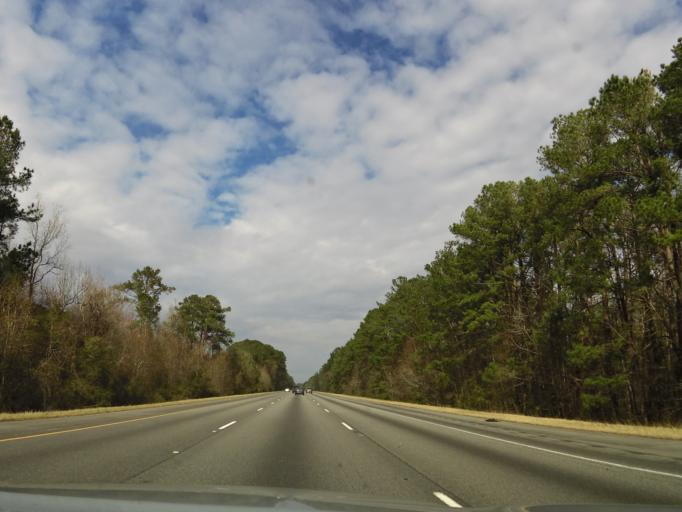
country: US
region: Georgia
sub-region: Bryan County
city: Richmond Hill
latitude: 31.8777
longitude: -81.3304
